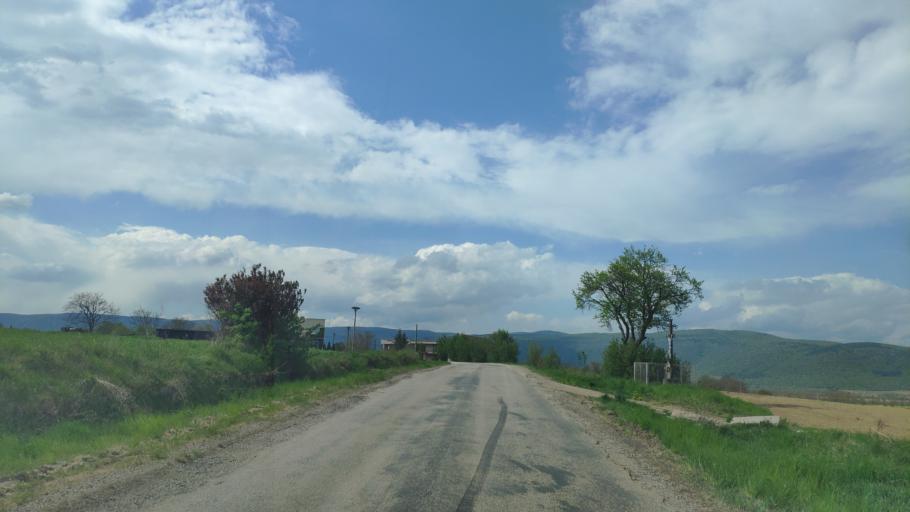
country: SK
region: Kosicky
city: Moldava nad Bodvou
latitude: 48.5796
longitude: 20.9288
